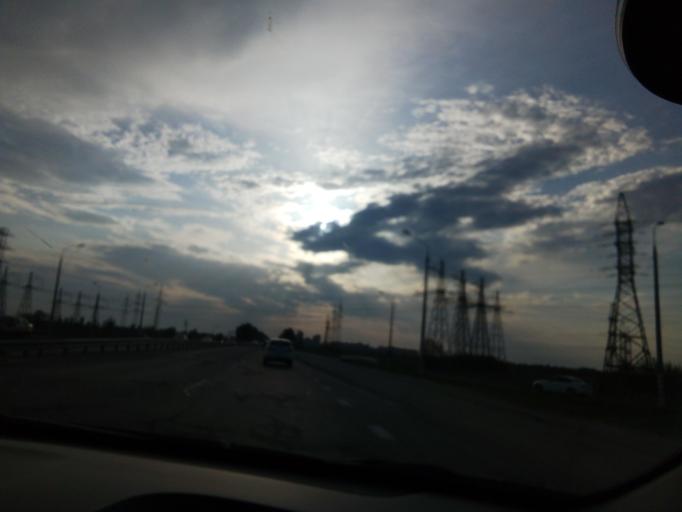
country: RU
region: Chuvashia
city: Novocheboksarsk
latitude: 56.1225
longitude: 47.4211
